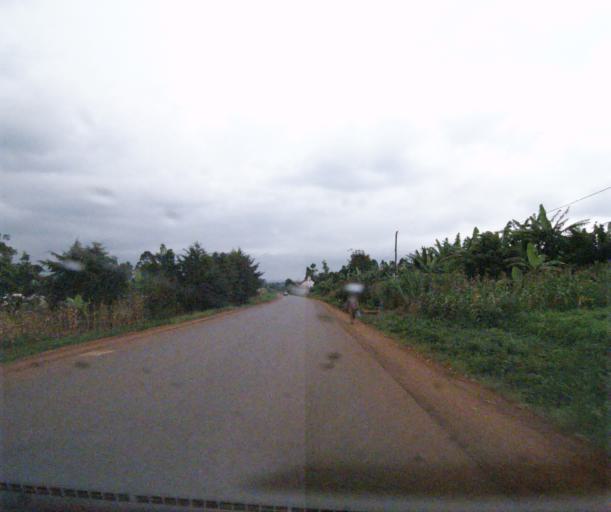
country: CM
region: West
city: Bansoa
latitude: 5.4876
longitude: 10.2035
